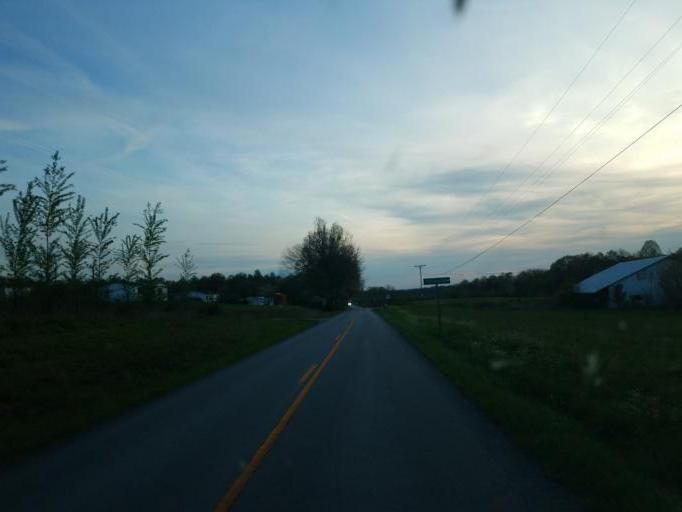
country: US
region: Kentucky
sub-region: Hart County
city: Munfordville
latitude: 37.2327
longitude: -85.7061
